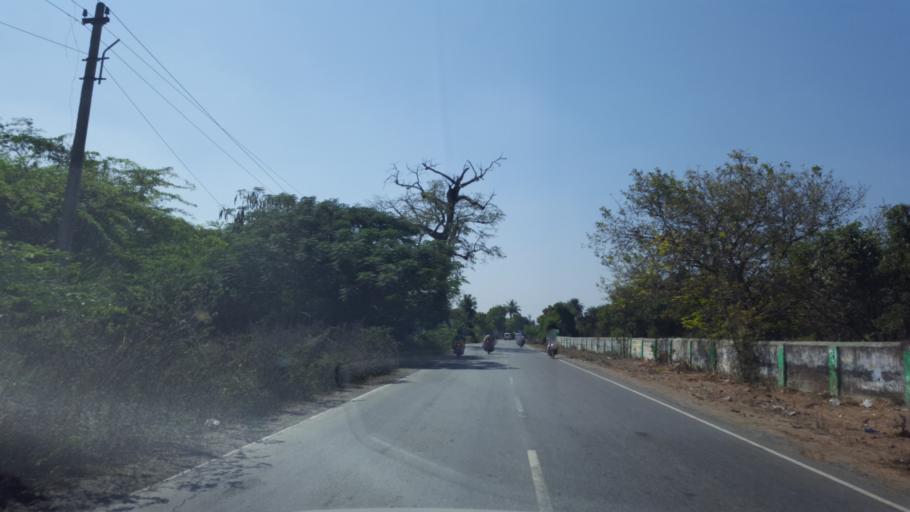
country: IN
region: Tamil Nadu
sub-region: Kancheepuram
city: Wallajahbad
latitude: 12.7854
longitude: 79.8332
